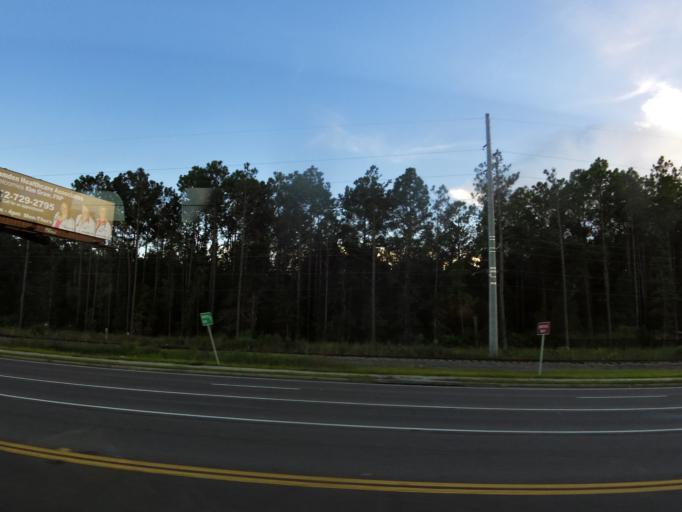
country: US
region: Georgia
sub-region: Camden County
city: St Marys
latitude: 30.7796
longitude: -81.6240
